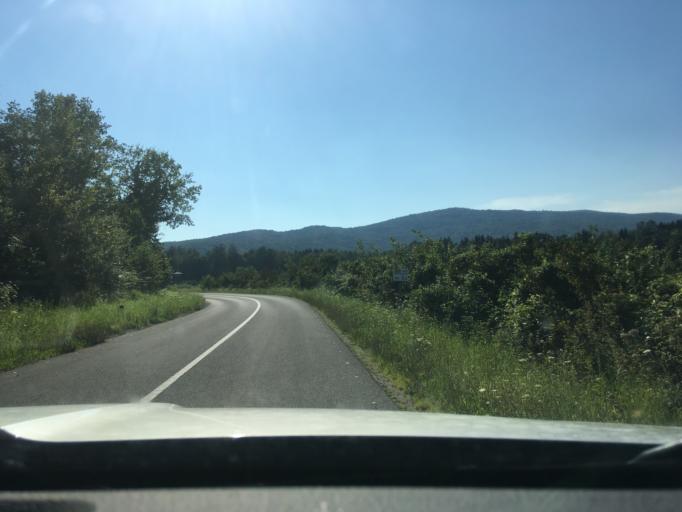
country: SI
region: Crnomelj
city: Crnomelj
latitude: 45.4567
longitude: 15.2197
